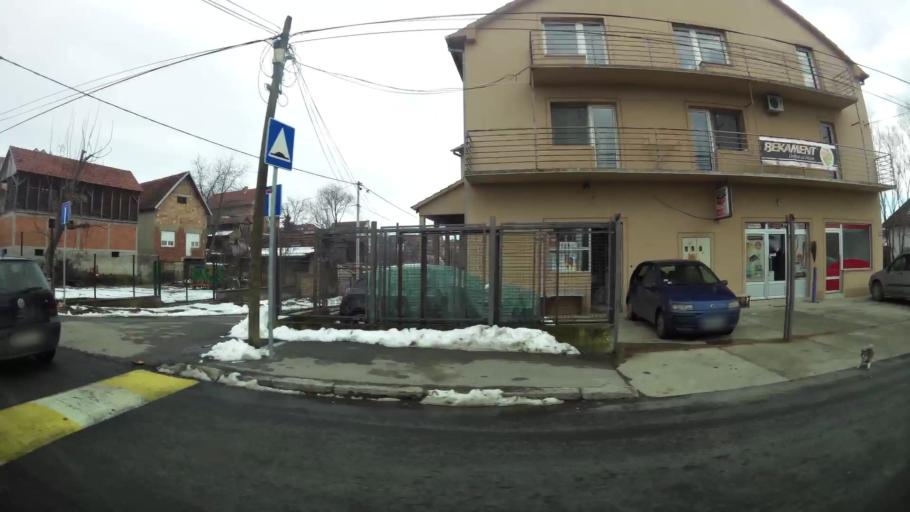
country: RS
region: Central Serbia
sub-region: Belgrade
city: Surcin
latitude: 44.7921
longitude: 20.2602
